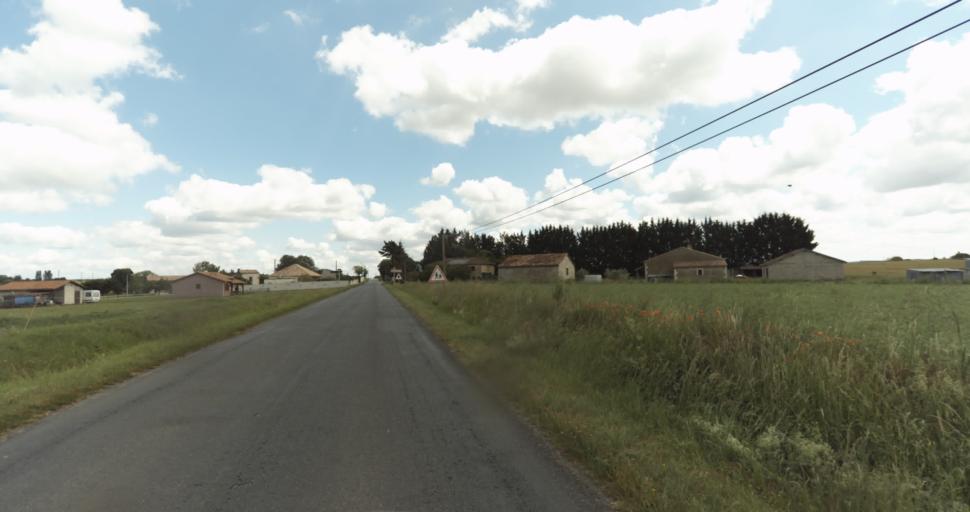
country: FR
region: Aquitaine
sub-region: Departement de la Dordogne
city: Beaumont-du-Perigord
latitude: 44.7574
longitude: 0.7195
